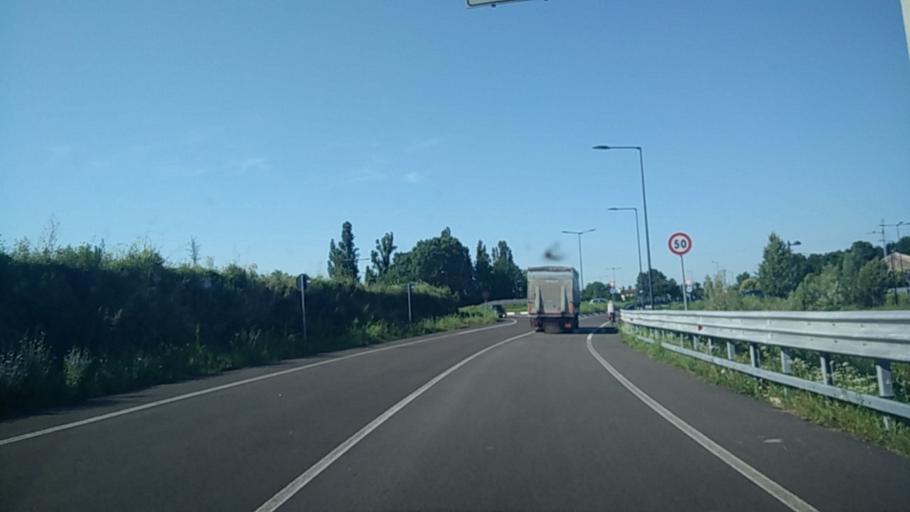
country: IT
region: Veneto
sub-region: Provincia di Venezia
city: Dolo
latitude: 45.4288
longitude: 12.0918
